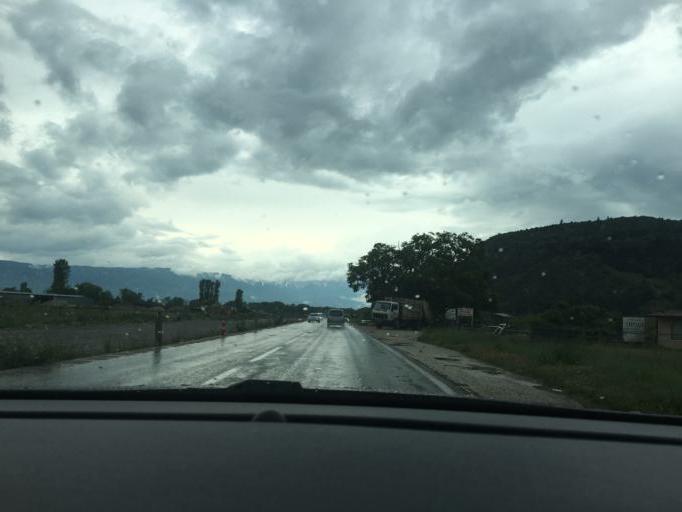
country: MK
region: Ohrid
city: Ohrid
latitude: 41.1368
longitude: 20.7707
